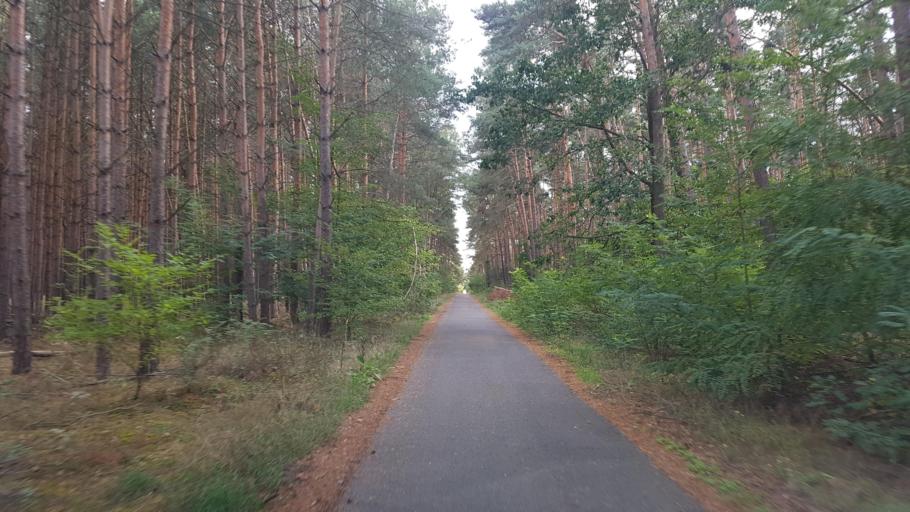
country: DE
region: Brandenburg
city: Ihlow
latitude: 51.8588
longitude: 13.2612
